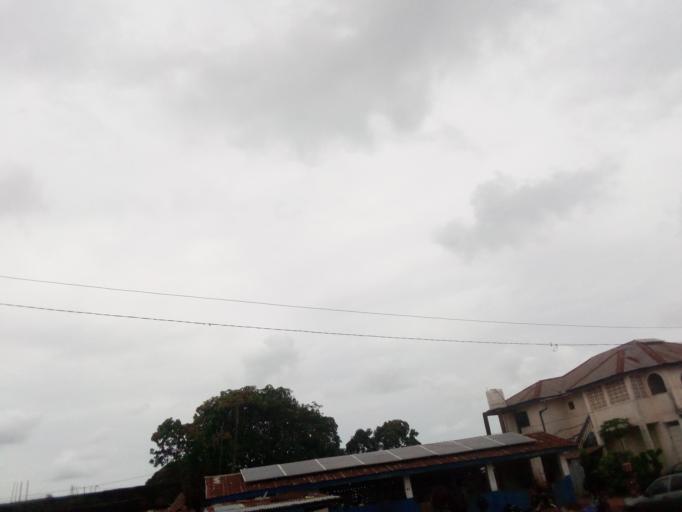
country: SL
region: Northern Province
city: Kambia
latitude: 9.1115
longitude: -12.9273
